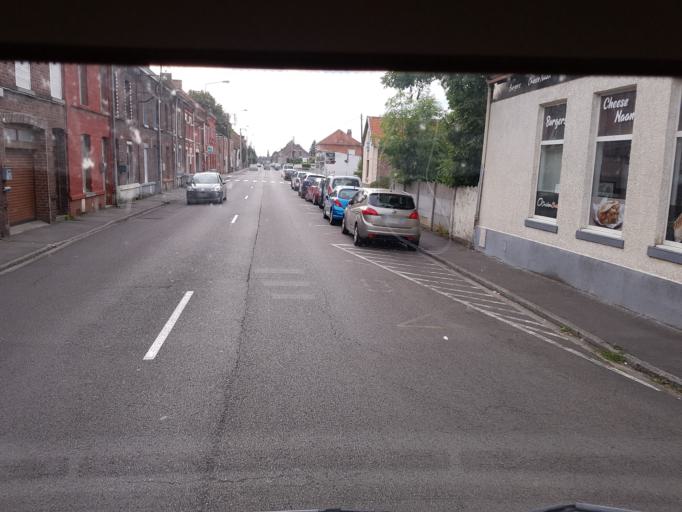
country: FR
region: Nord-Pas-de-Calais
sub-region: Departement du Nord
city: Conde-sur-l'Escaut
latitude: 50.4556
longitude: 3.5855
